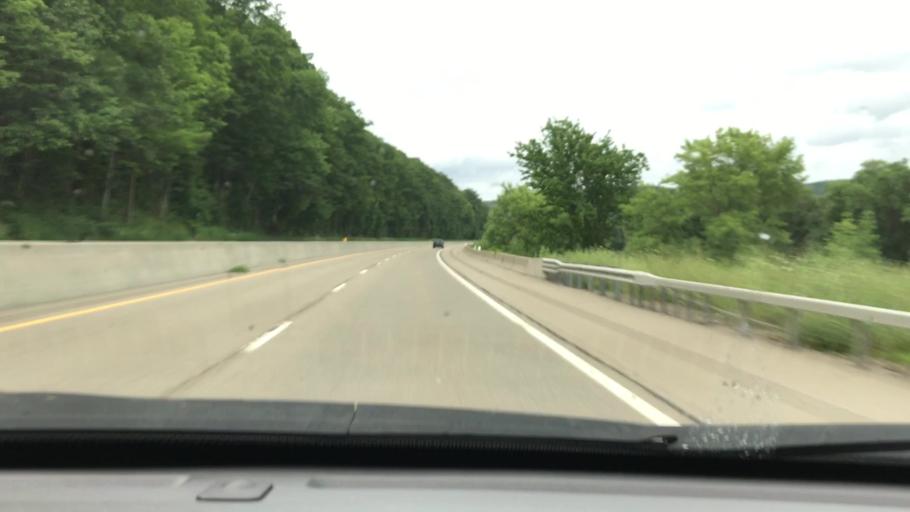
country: US
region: New York
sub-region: Cattaraugus County
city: Salamanca
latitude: 42.1289
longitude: -78.6665
